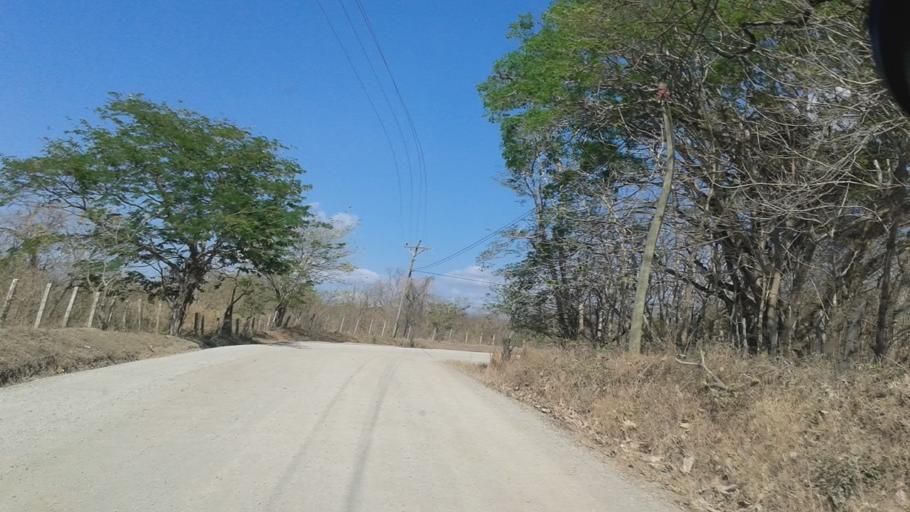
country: CR
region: Guanacaste
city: Santa Cruz
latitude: 10.1160
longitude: -85.7861
